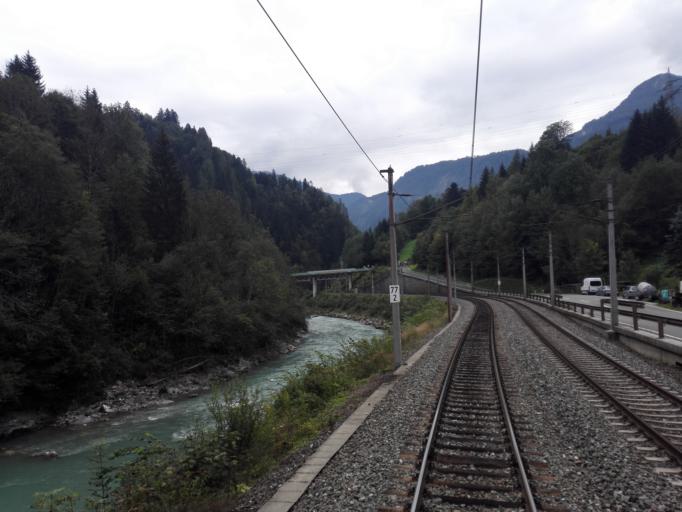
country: AT
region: Salzburg
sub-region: Politischer Bezirk Zell am See
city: Lend
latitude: 47.3060
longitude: 13.0307
